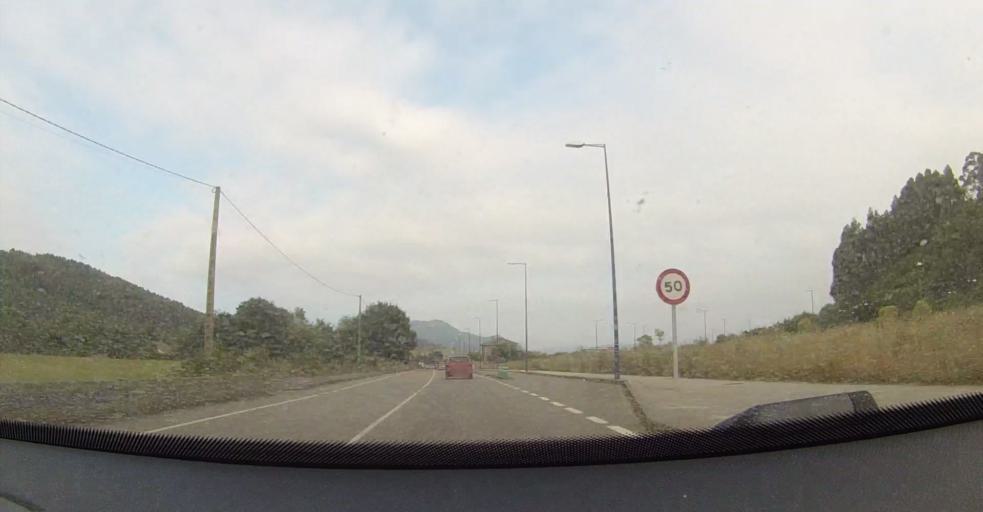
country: ES
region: Cantabria
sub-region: Provincia de Cantabria
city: Argonos
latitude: 43.4581
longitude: -3.5047
